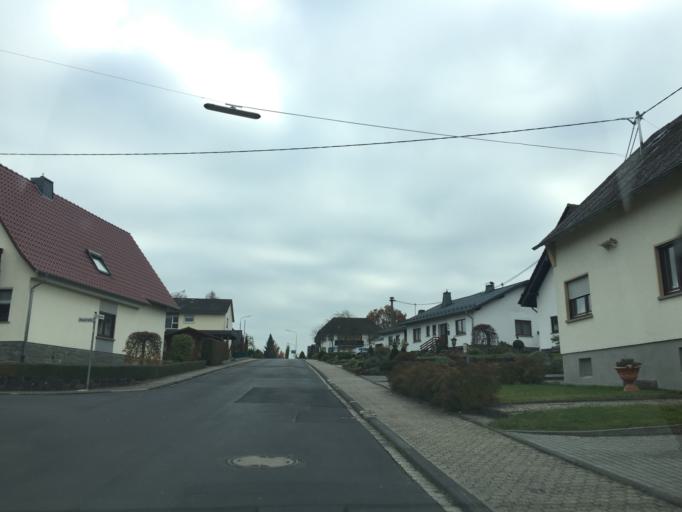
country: DE
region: Rheinland-Pfalz
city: Heiligenroth
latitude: 50.4480
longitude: 7.8599
